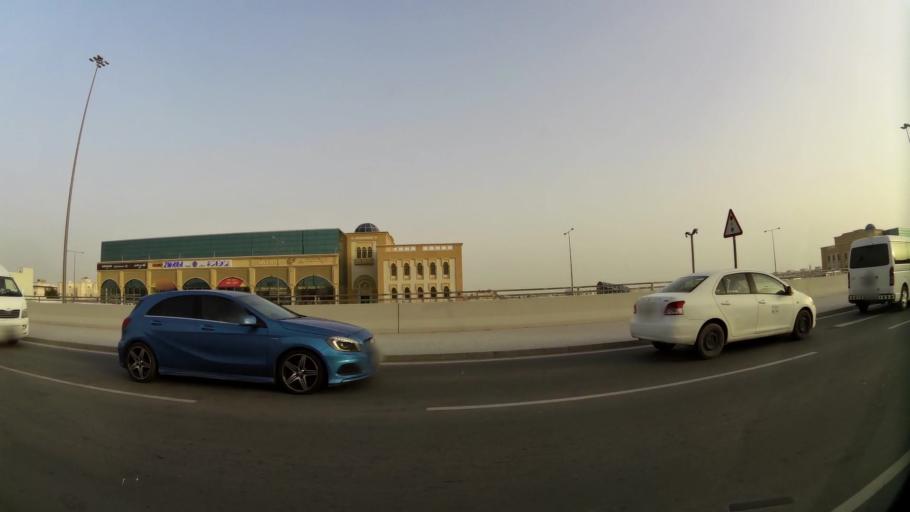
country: QA
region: Baladiyat ar Rayyan
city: Ar Rayyan
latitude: 25.2350
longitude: 51.4476
